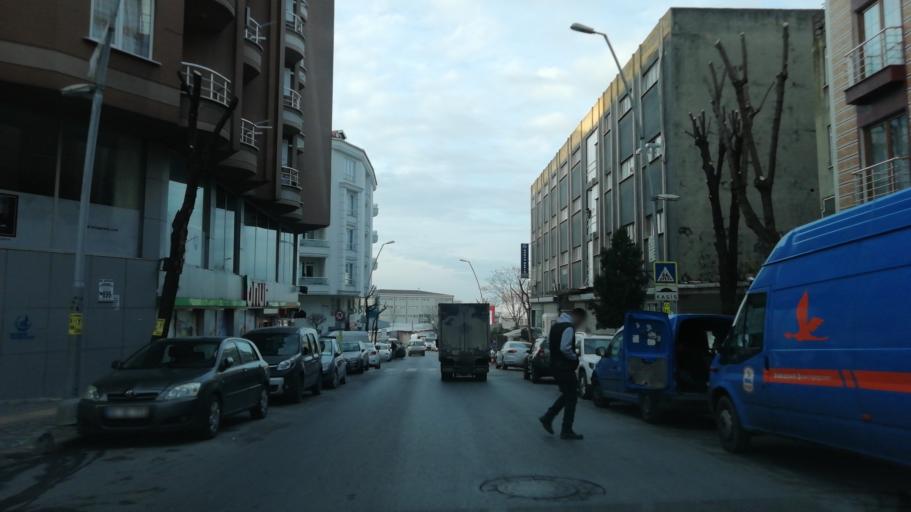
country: TR
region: Istanbul
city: Bahcelievler
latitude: 41.0051
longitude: 28.8271
